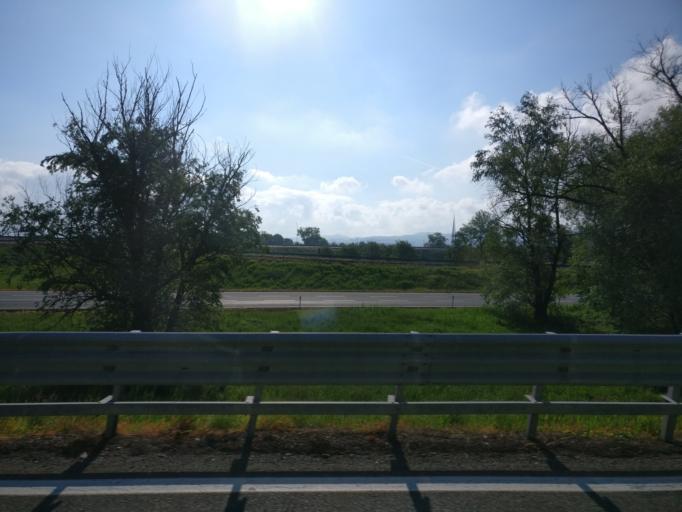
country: IT
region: Piedmont
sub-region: Provincia di Torino
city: Settimo Torinese
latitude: 45.1334
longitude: 7.7262
